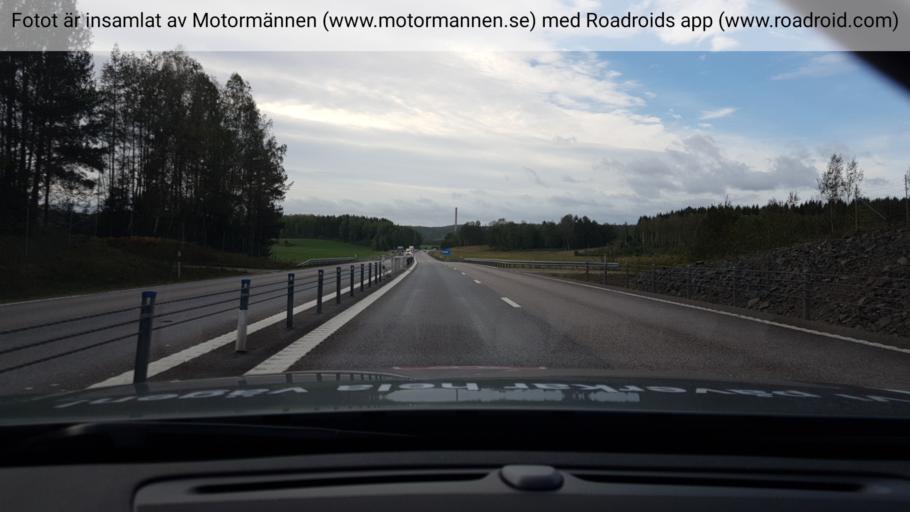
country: SE
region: Vaermland
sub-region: Karlstads Kommun
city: Valberg
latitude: 59.3809
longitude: 13.2061
